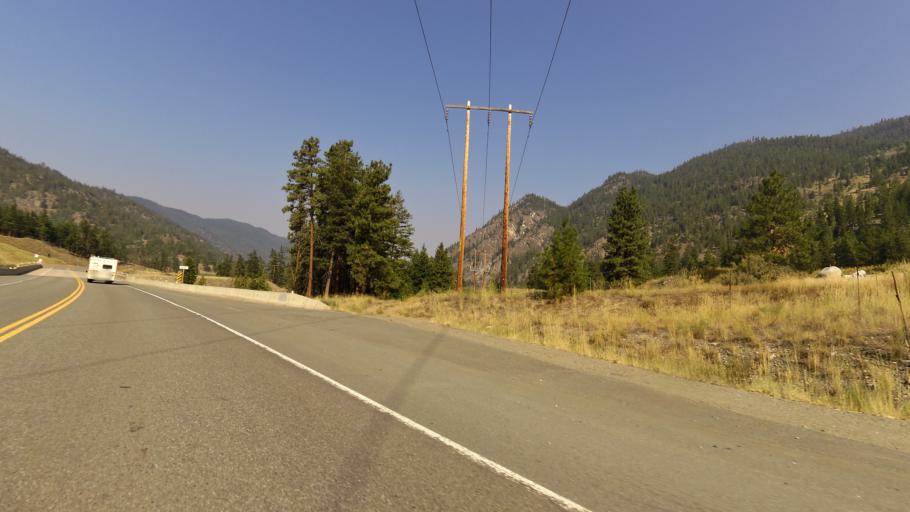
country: CA
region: British Columbia
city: Princeton
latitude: 49.3779
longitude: -120.1516
